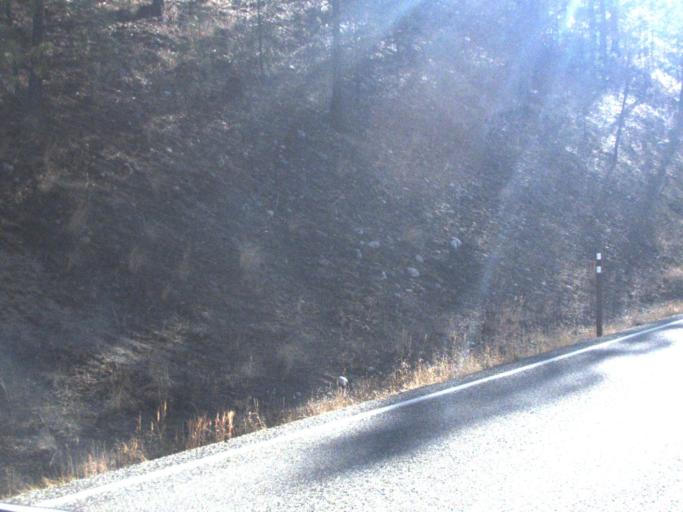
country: CA
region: British Columbia
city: Grand Forks
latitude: 48.8610
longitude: -118.6048
